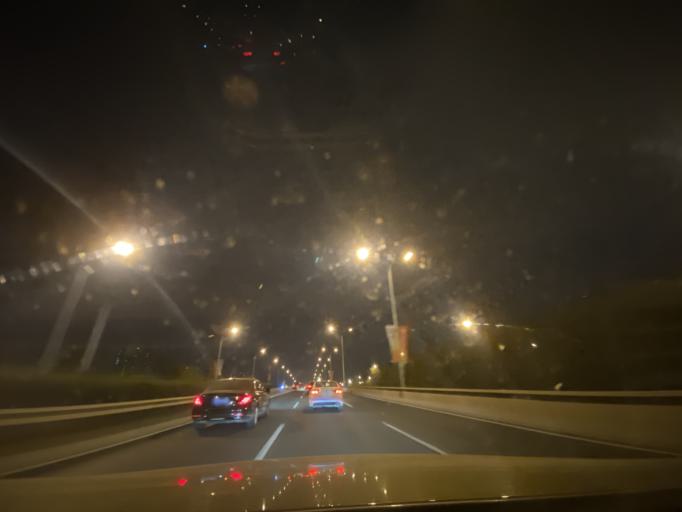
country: CN
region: Beijing
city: Lugouqiao
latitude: 39.8958
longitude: 116.2804
